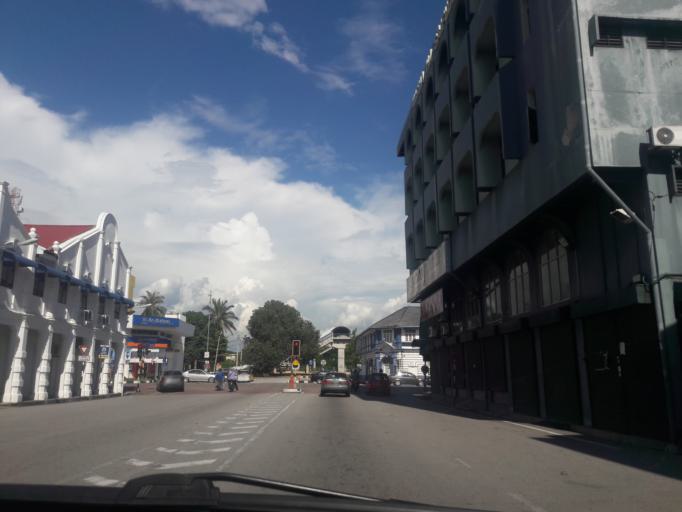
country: MY
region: Kedah
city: Sungai Petani
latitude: 5.6414
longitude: 100.4883
